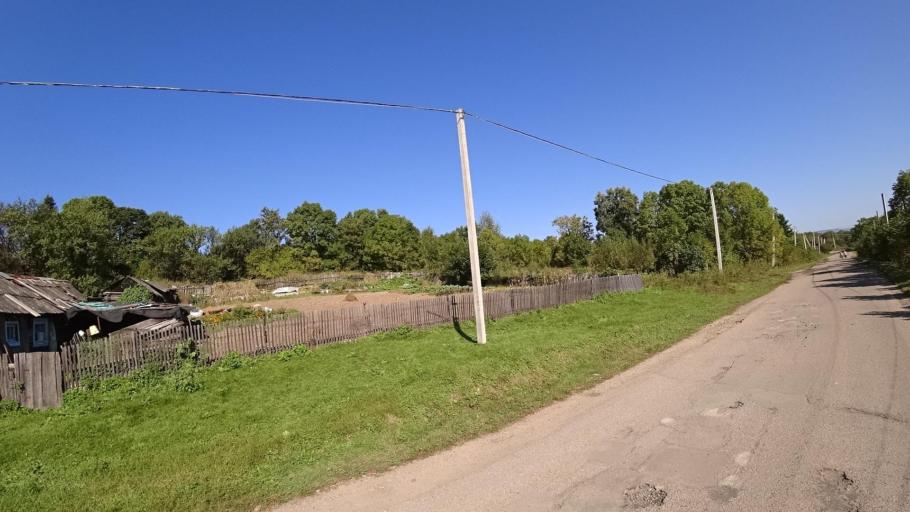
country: RU
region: Jewish Autonomous Oblast
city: Bira
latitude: 49.0088
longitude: 132.4725
